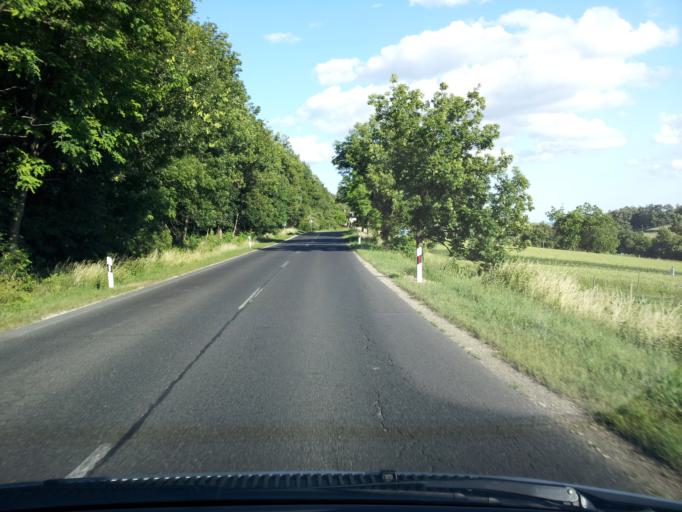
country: HU
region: Veszprem
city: Zirc
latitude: 47.2155
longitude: 17.9078
